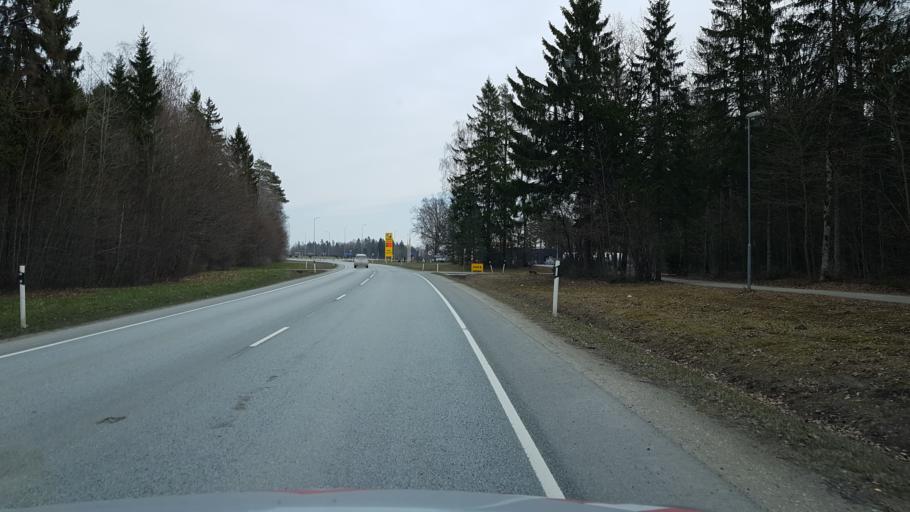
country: EE
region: Laeaene-Virumaa
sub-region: Rakvere linn
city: Rakvere
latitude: 59.3206
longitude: 26.3662
